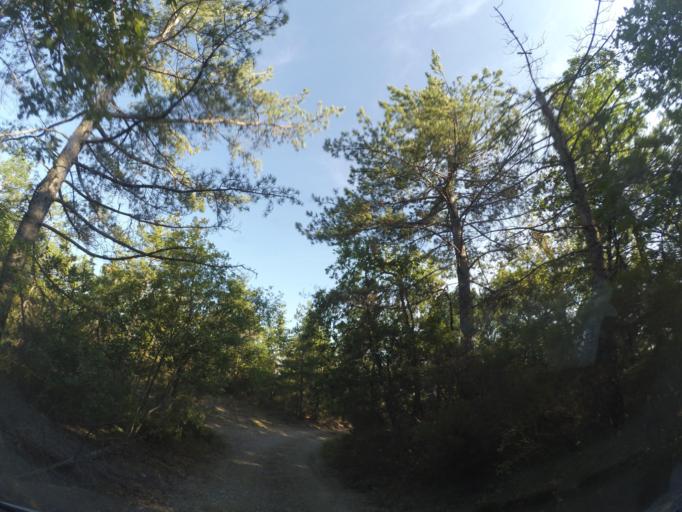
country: IT
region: Tuscany
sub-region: Province of Arezzo
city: Castiglion Fibocchi
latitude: 43.5477
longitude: 11.7881
